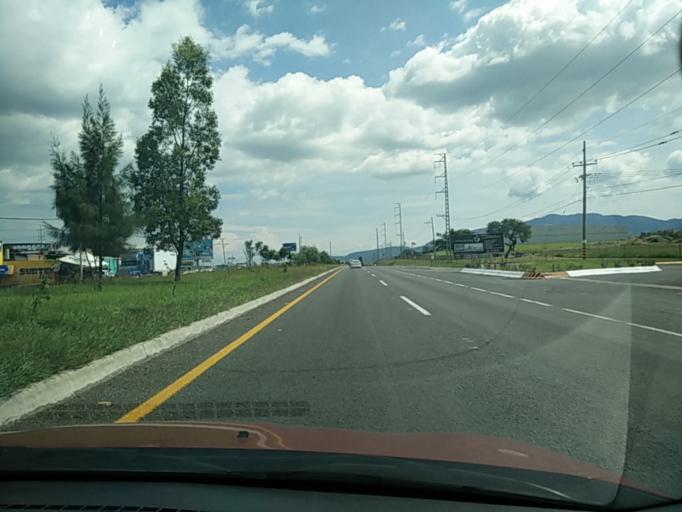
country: MX
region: Jalisco
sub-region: Ixtlahuacan de los Membrillos
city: Los Olivos
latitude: 20.4379
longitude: -103.2434
